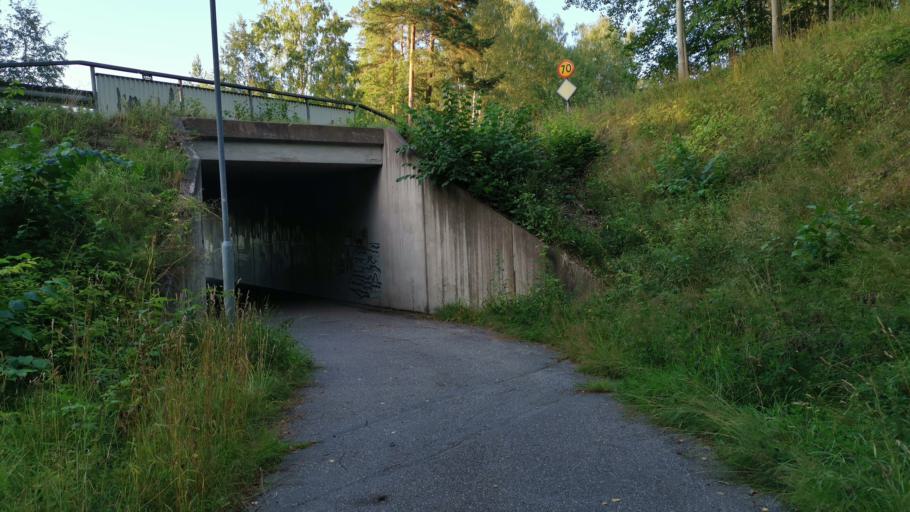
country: SE
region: OEstergoetland
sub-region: Norrkopings Kommun
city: Krokek
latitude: 58.7258
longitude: 16.4289
